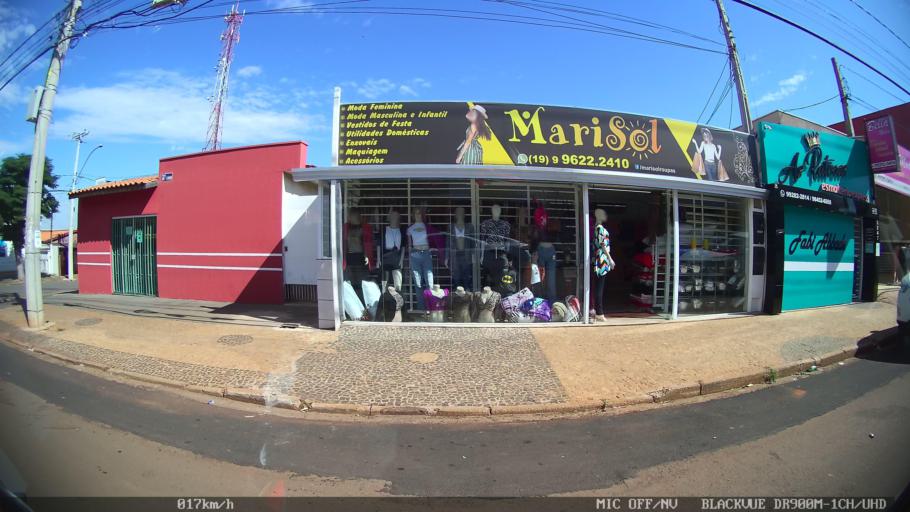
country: BR
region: Sao Paulo
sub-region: Santa Barbara D'Oeste
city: Santa Barbara d'Oeste
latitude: -22.7388
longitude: -47.3796
